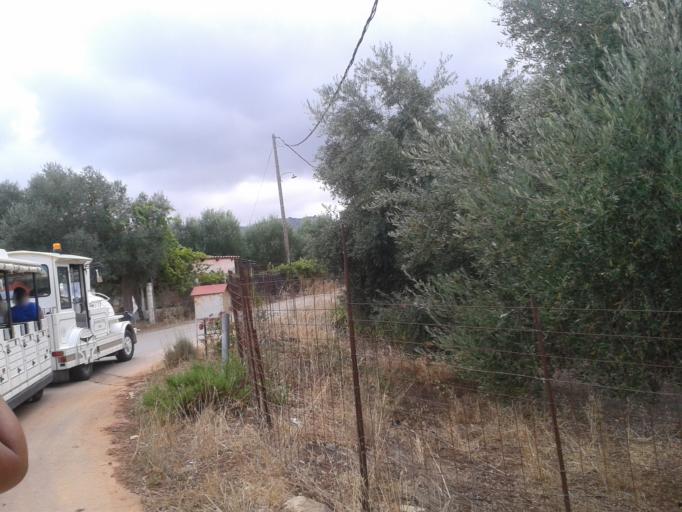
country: GR
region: Crete
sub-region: Nomos Chanias
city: Perivolia
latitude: 35.4857
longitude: 23.9833
